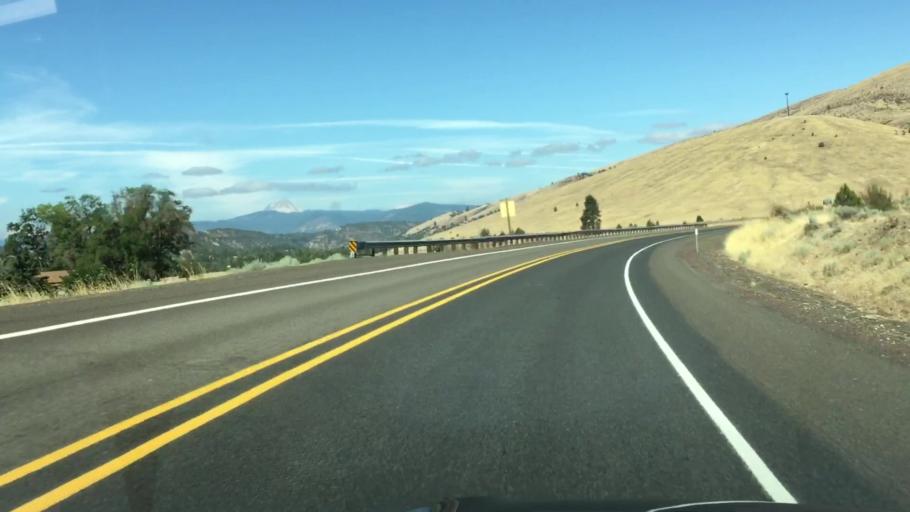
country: US
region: Oregon
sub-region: Wasco County
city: The Dalles
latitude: 45.2553
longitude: -121.1857
